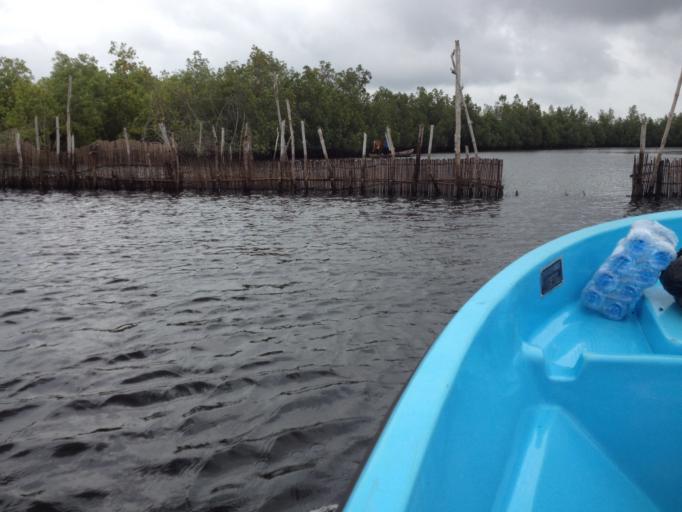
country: BJ
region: Mono
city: Come
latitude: 6.3767
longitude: 1.9367
